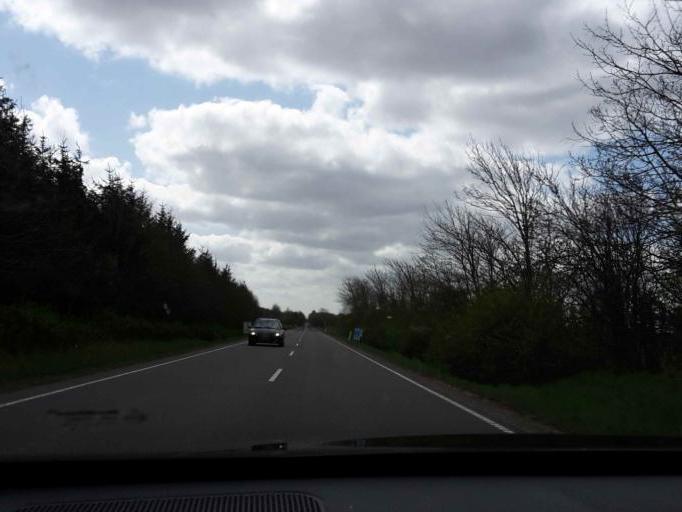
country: DK
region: South Denmark
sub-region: Varde Kommune
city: Olgod
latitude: 55.7069
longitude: 8.6079
